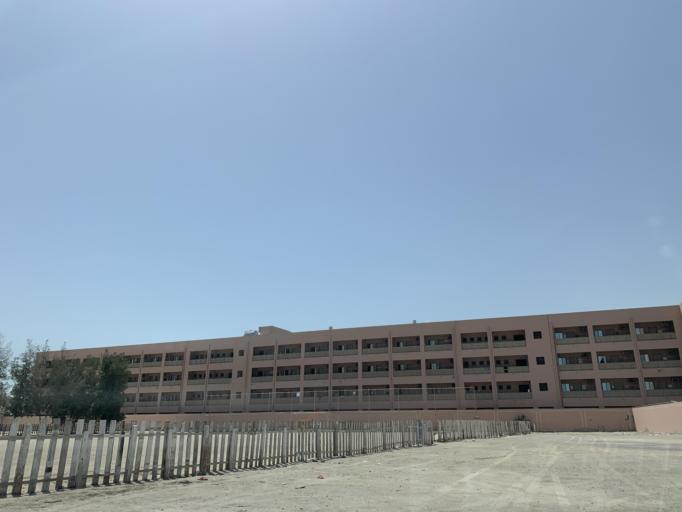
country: BH
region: Northern
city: Sitrah
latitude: 26.1418
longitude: 50.6125
